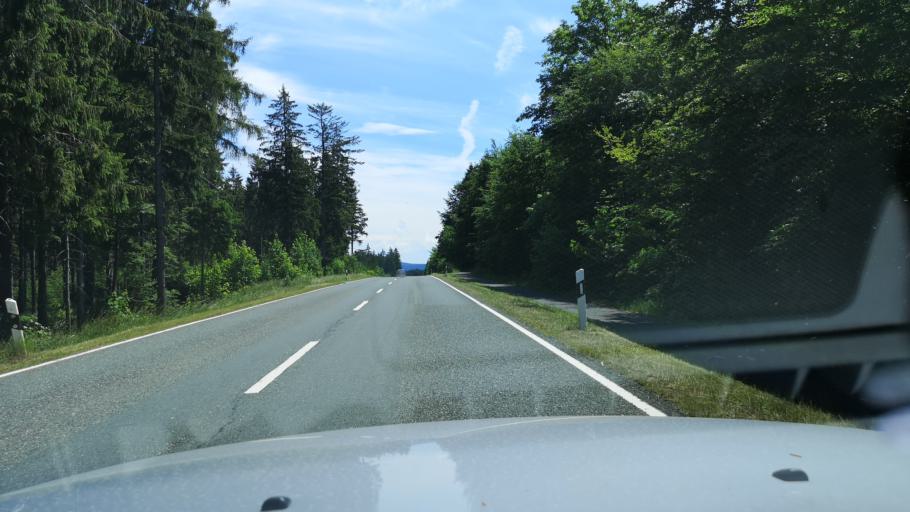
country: DE
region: Thuringia
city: Grafenthal
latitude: 50.4683
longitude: 11.3202
